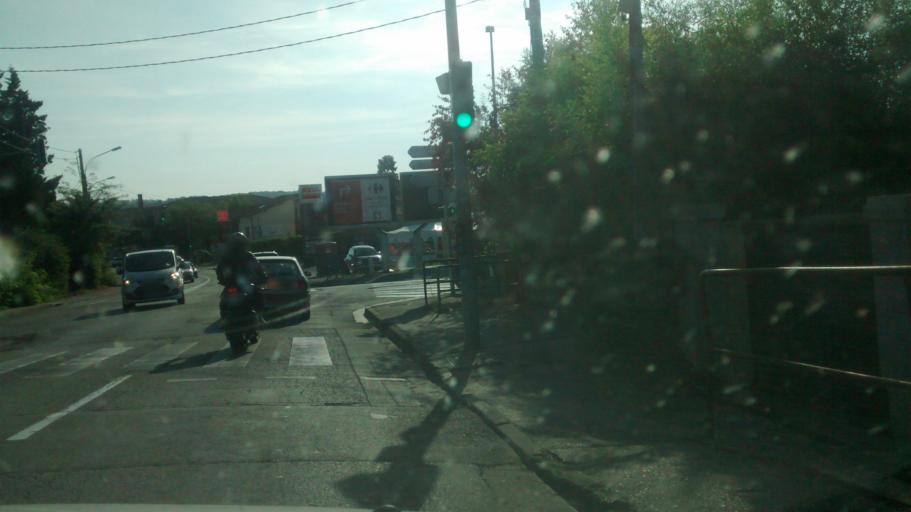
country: FR
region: Midi-Pyrenees
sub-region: Departement de la Haute-Garonne
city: Balma
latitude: 43.6050
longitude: 1.4782
